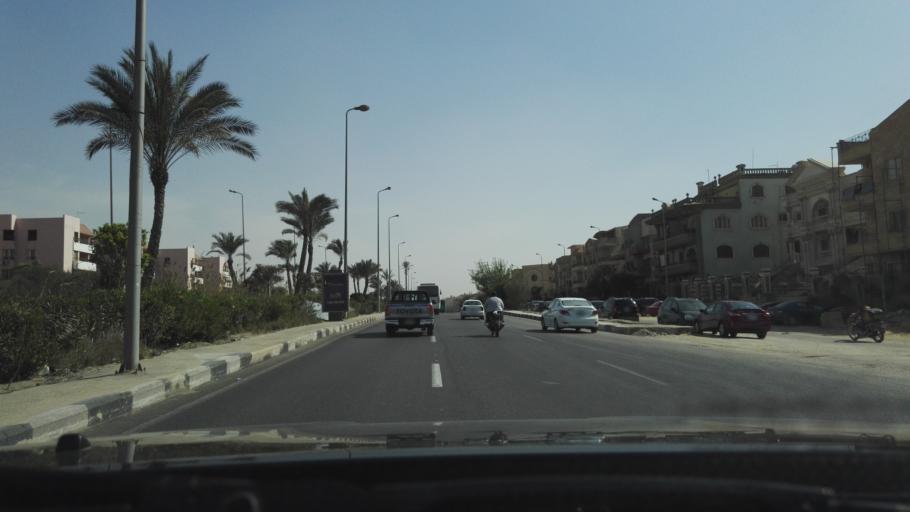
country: EG
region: Muhafazat al Qalyubiyah
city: Al Khankah
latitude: 30.0633
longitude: 31.4747
